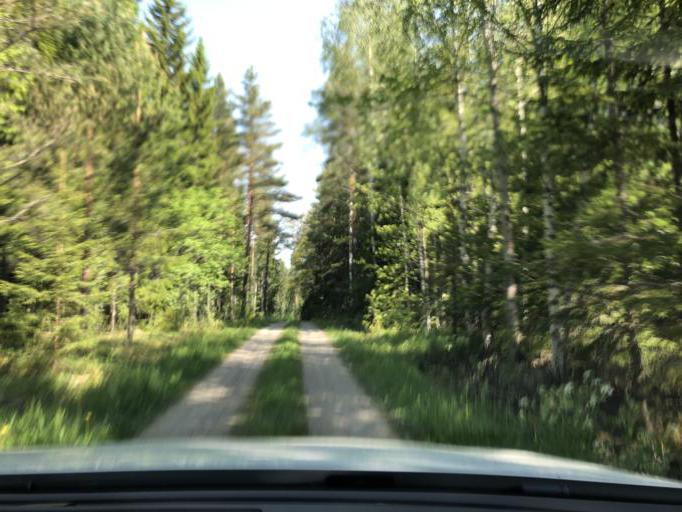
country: SE
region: Dalarna
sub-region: Avesta Kommun
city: Horndal
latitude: 60.2147
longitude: 16.4931
